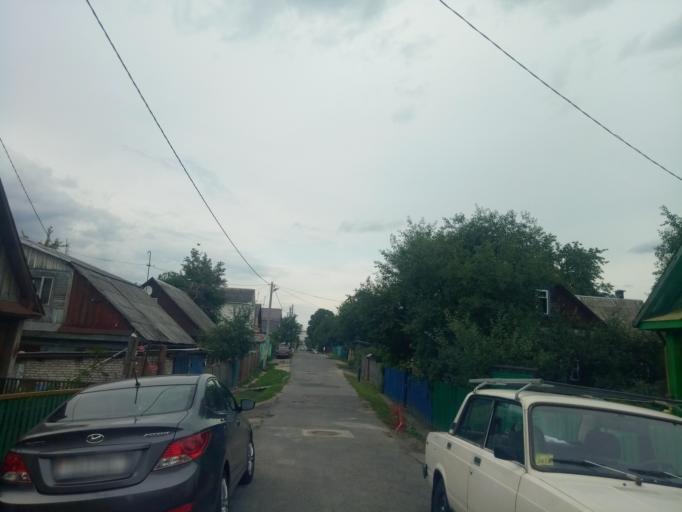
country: BY
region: Minsk
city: Minsk
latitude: 53.9017
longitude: 27.5116
